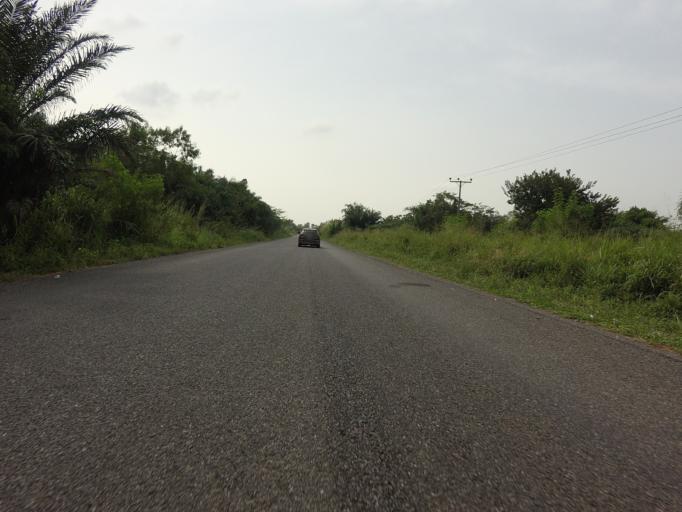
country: GH
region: Volta
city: Ho
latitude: 6.4294
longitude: 0.1905
